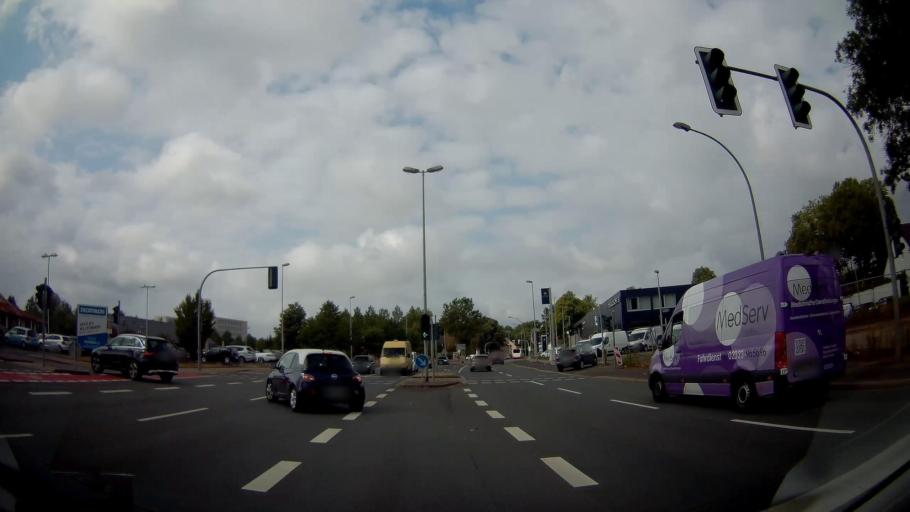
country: DE
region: North Rhine-Westphalia
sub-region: Regierungsbezirk Arnsberg
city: Herne
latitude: 51.5296
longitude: 7.2012
